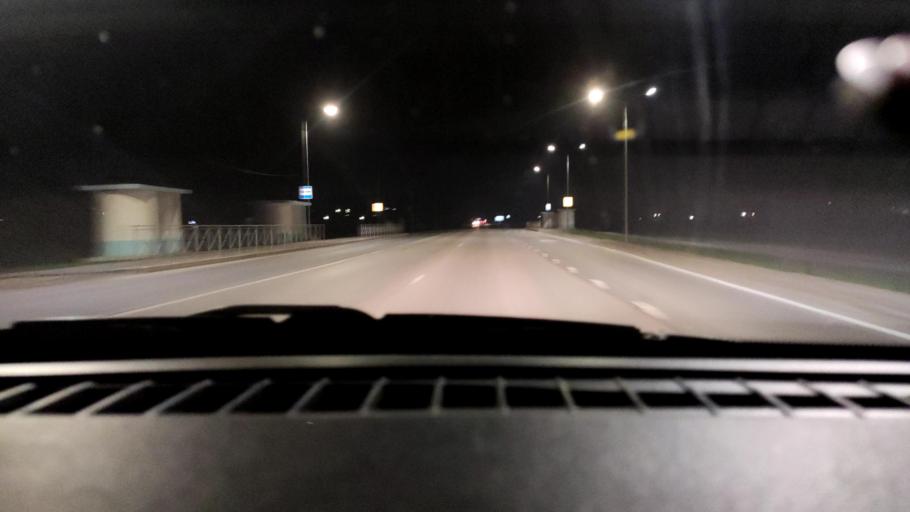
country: RU
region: Perm
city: Kultayevo
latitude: 57.8708
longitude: 55.8672
